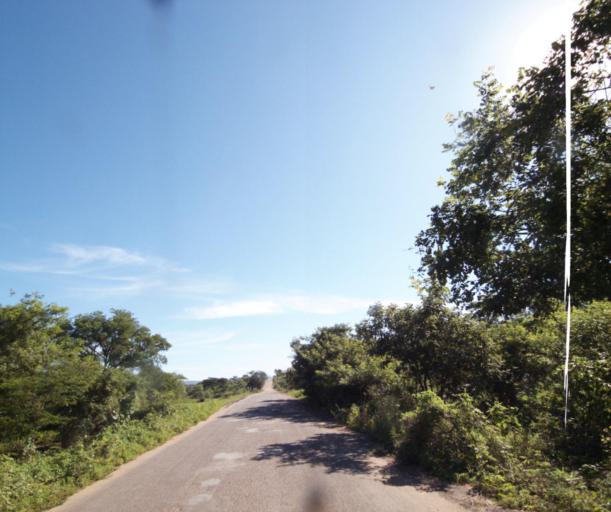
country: BR
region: Bahia
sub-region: Sao Felix Do Coribe
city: Santa Maria da Vitoria
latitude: -13.6382
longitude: -44.4360
